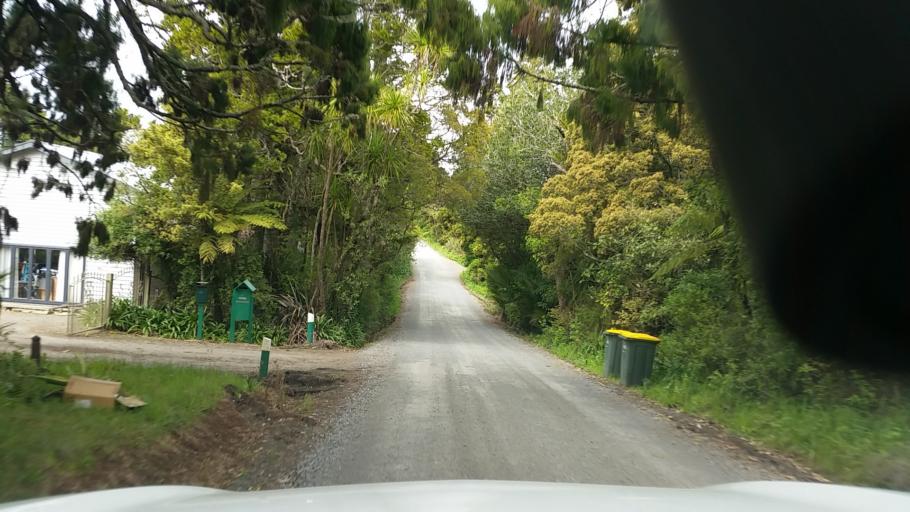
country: NZ
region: Auckland
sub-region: Auckland
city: Muriwai Beach
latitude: -36.8454
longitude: 174.5105
